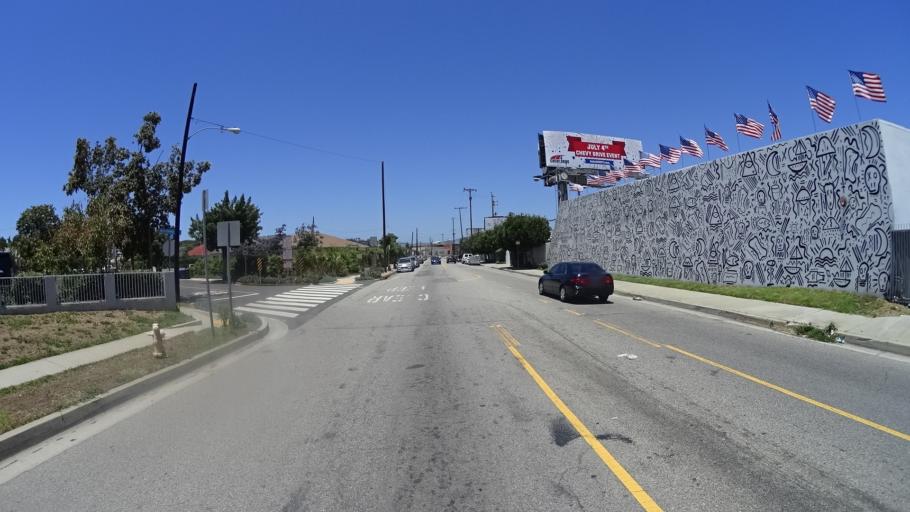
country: US
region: California
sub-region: Los Angeles County
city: Westwood, Los Angeles
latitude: 34.0290
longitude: -118.4553
